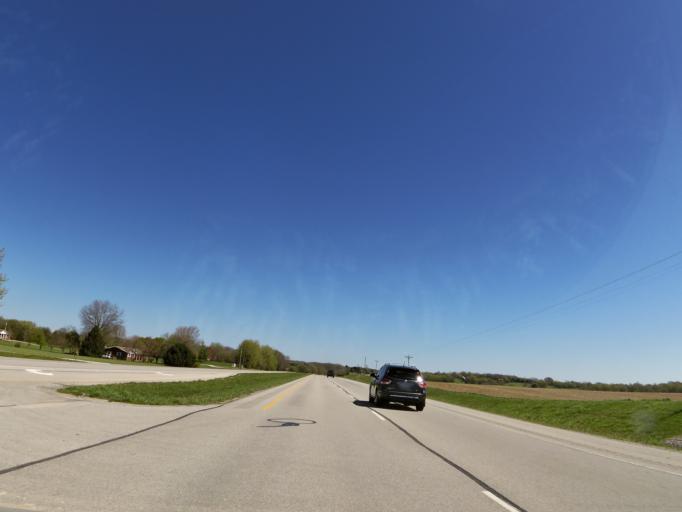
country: US
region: Kentucky
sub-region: Logan County
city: Auburn
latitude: 36.9041
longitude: -86.5892
